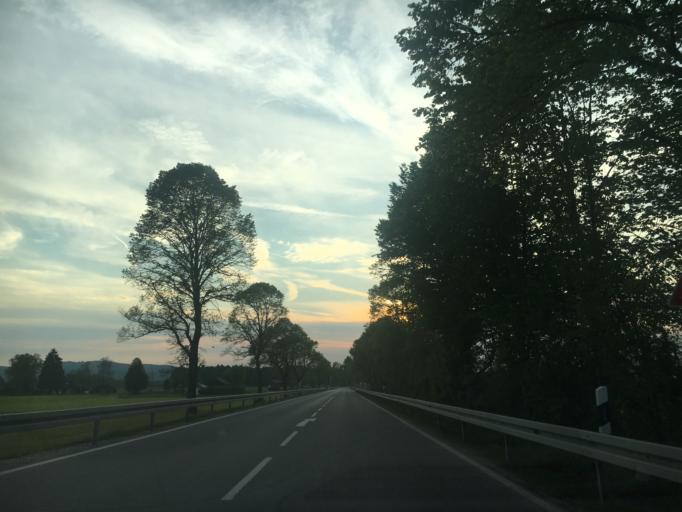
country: DE
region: Bavaria
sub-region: Upper Bavaria
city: Bichl
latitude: 47.7169
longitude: 11.4090
